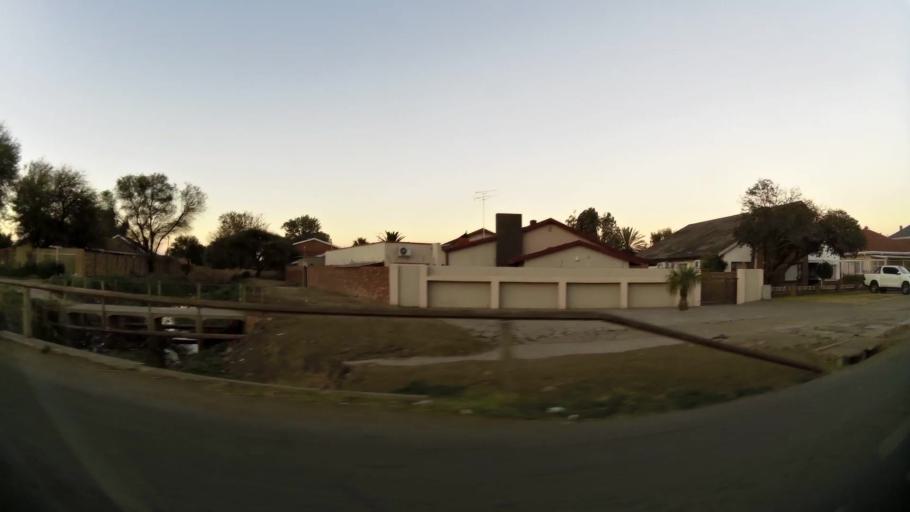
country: ZA
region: Northern Cape
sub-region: Frances Baard District Municipality
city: Kimberley
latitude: -28.7211
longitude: 24.7735
